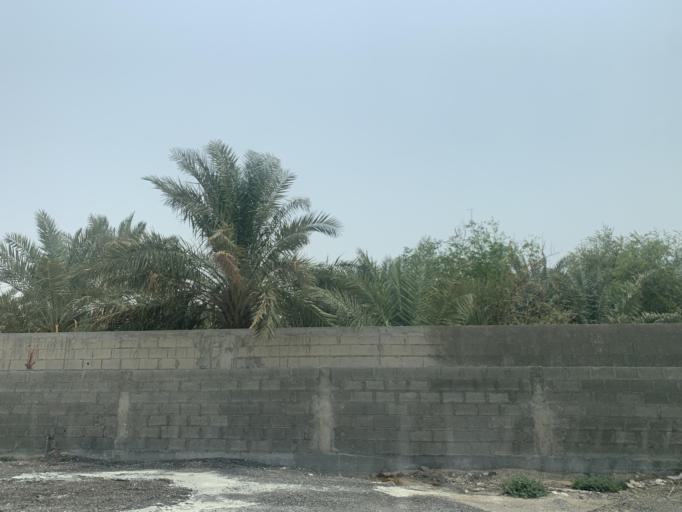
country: BH
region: Central Governorate
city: Madinat Hamad
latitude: 26.1689
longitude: 50.4697
